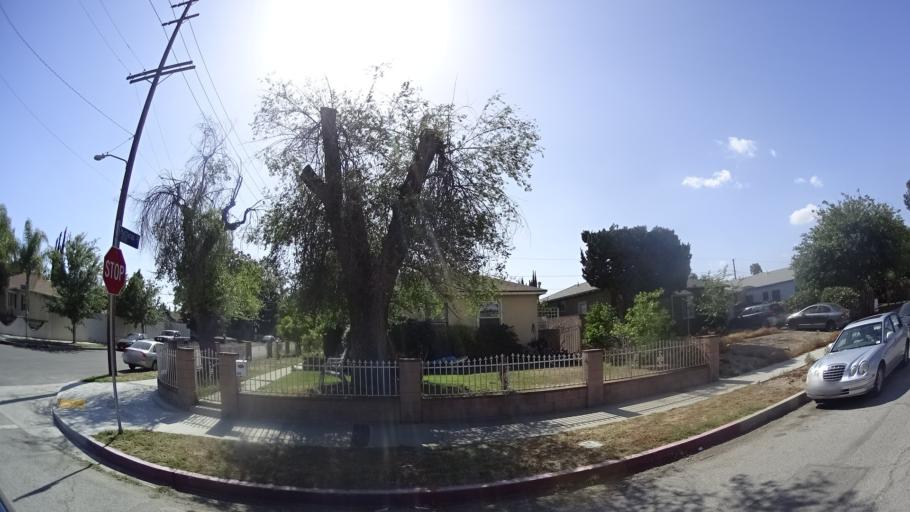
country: US
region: California
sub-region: Los Angeles County
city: North Hollywood
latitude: 34.1759
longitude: -118.3637
